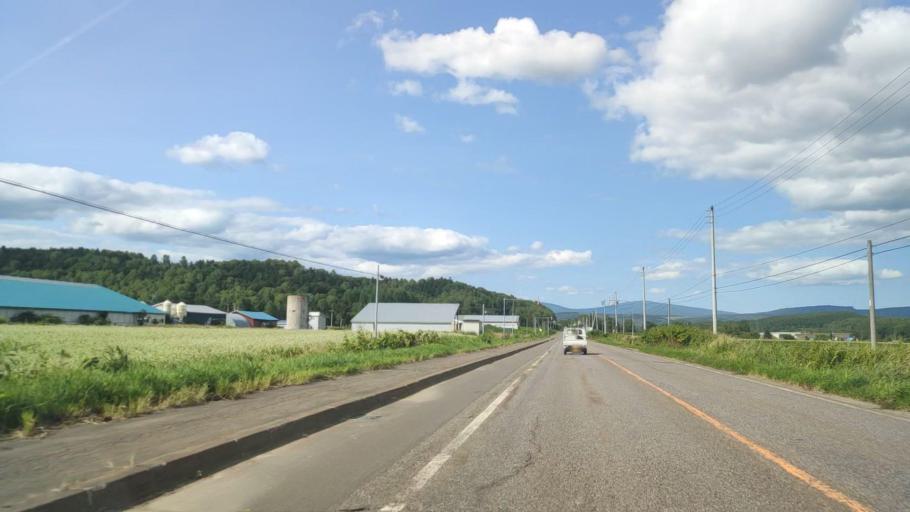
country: JP
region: Hokkaido
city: Nayoro
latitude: 44.3997
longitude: 142.3957
